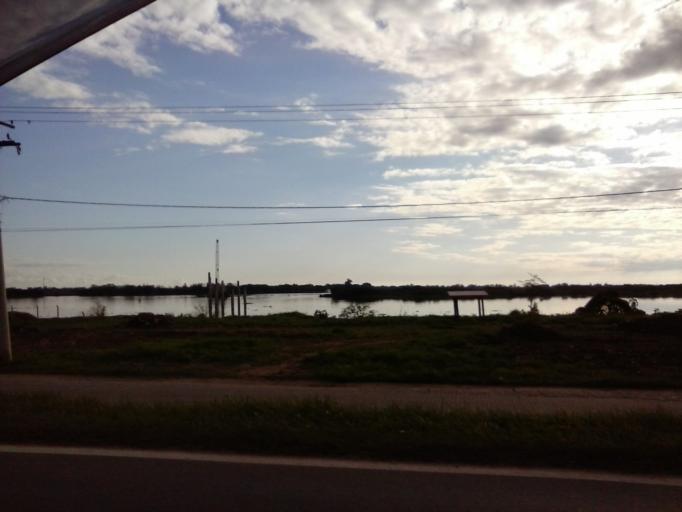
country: BR
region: Rio Grande do Sul
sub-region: Porto Alegre
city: Porto Alegre
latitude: -29.9870
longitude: -51.2032
